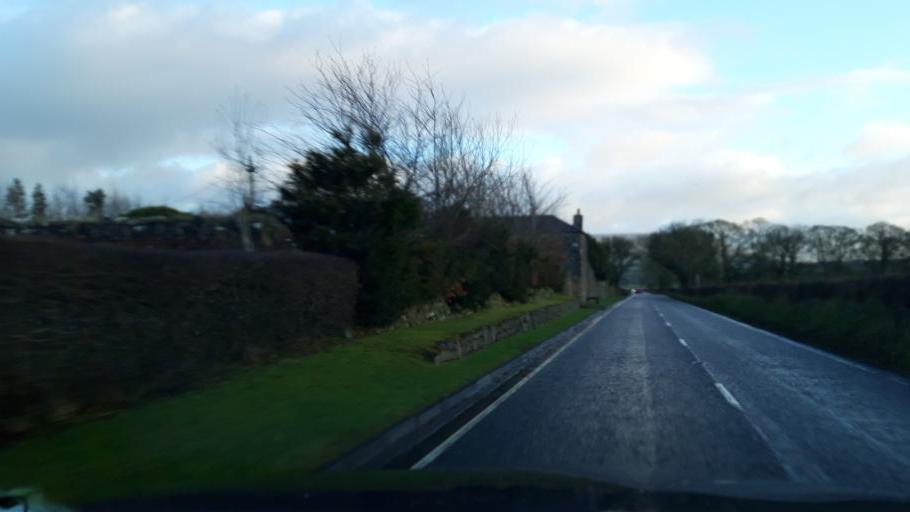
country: GB
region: Northern Ireland
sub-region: Moyle District
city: Ballycastle
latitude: 55.1193
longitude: -6.3286
